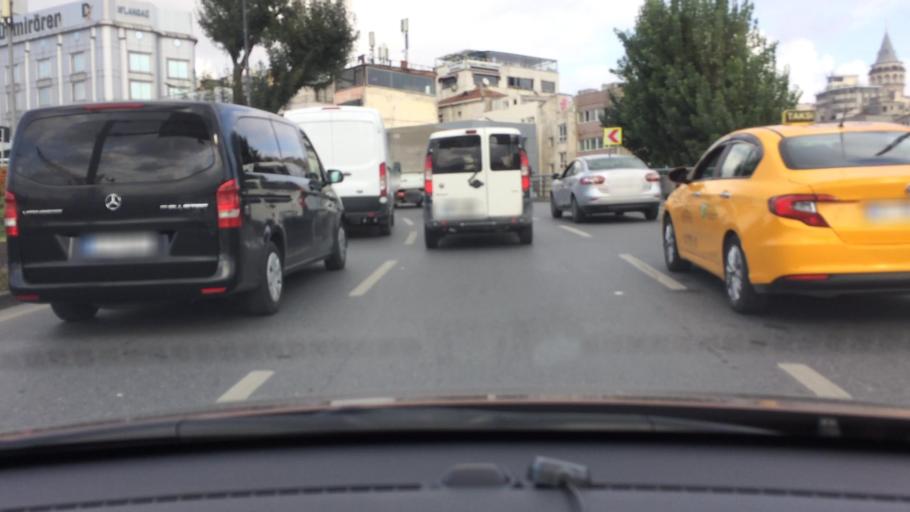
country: TR
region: Istanbul
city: Eminoenue
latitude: 41.0255
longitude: 28.9682
